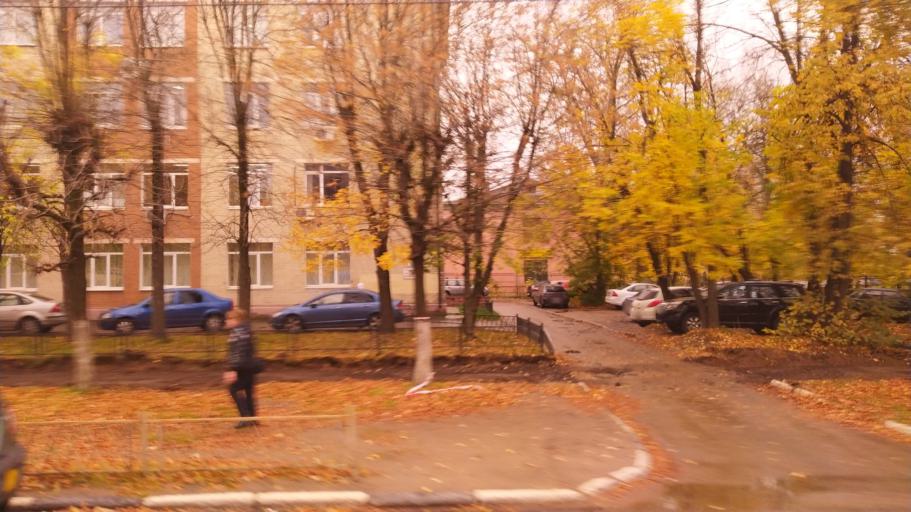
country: RU
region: Tverskaya
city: Tver
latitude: 56.8423
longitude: 35.9239
